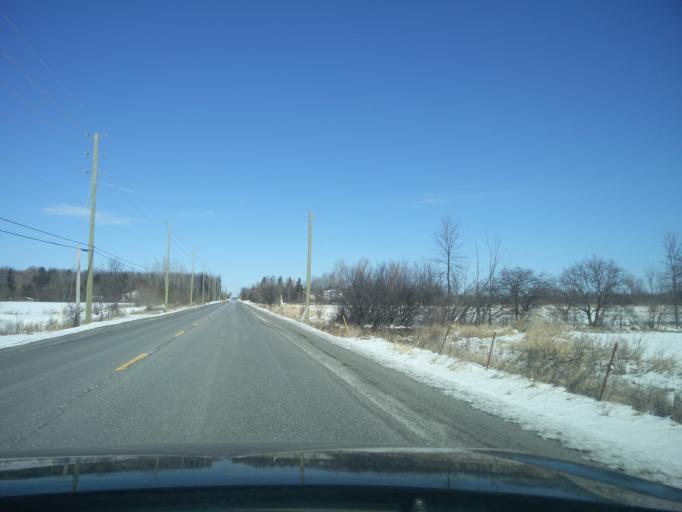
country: CA
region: Ontario
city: Bells Corners
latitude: 45.2283
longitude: -75.7215
